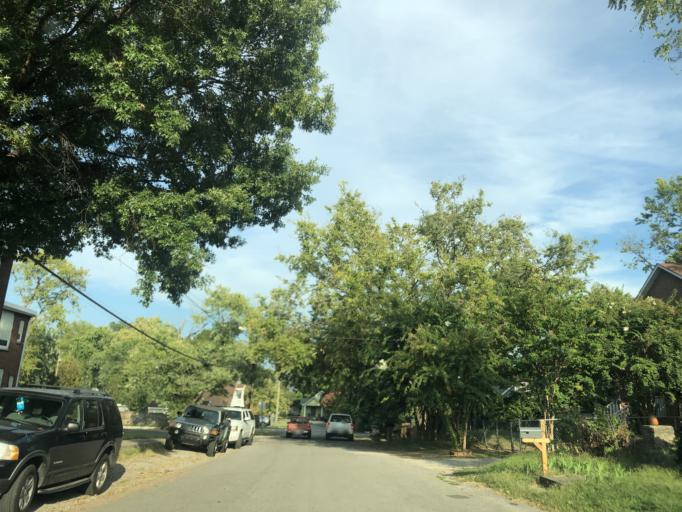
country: US
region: Tennessee
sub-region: Davidson County
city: Oak Hill
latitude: 36.1221
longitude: -86.7442
